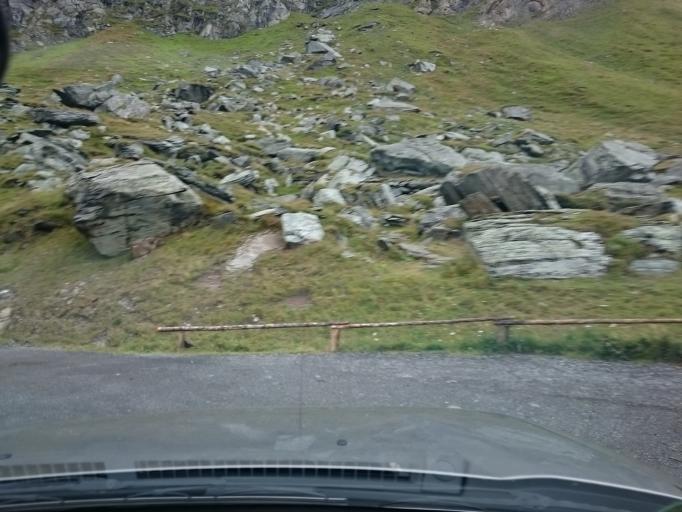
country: AT
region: Carinthia
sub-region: Politischer Bezirk Spittal an der Drau
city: Heiligenblut
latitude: 47.0803
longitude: 12.7658
